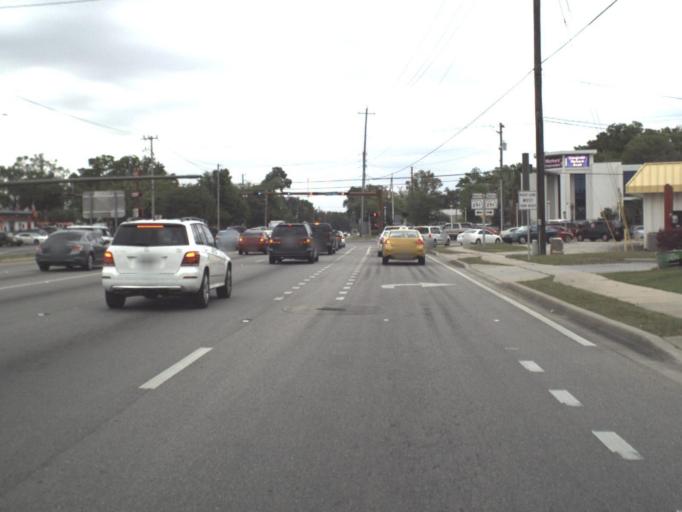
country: US
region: Florida
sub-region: Escambia County
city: Brent
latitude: 30.4729
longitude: -87.2263
